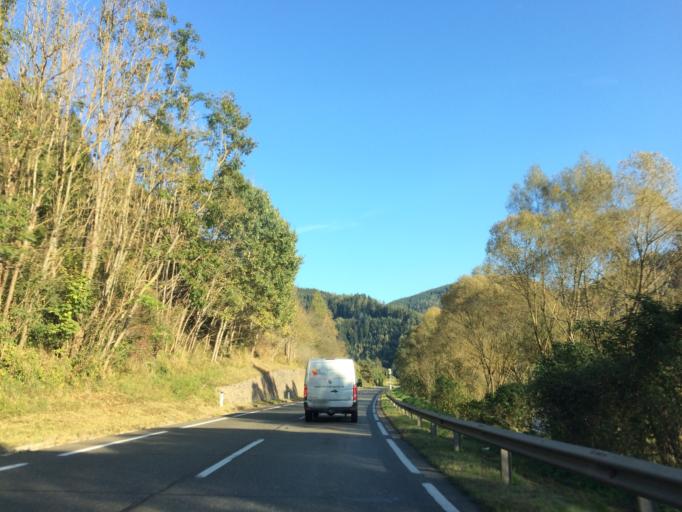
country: AT
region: Styria
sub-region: Politischer Bezirk Leoben
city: Sankt Michael in Obersteiermark
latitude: 47.3414
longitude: 15.0380
